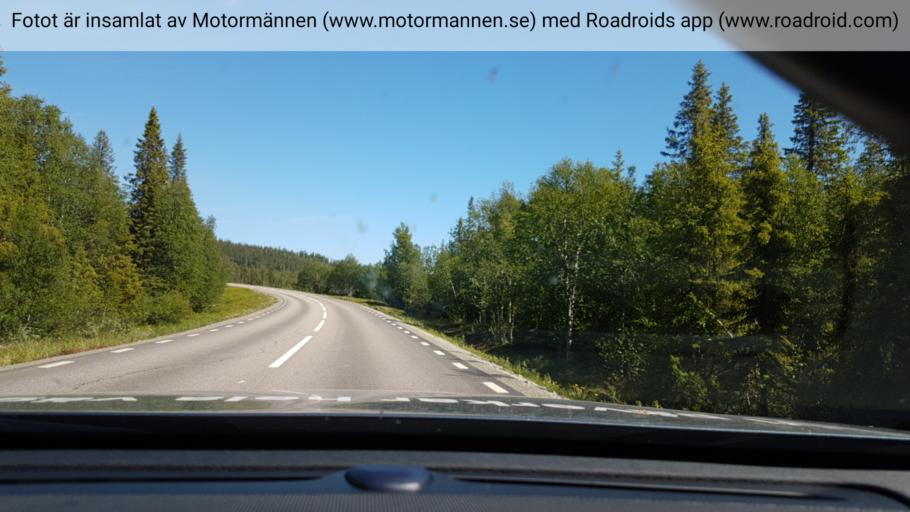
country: SE
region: Vaesterbotten
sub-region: Asele Kommun
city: Insjon
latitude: 64.7275
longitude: 17.4987
